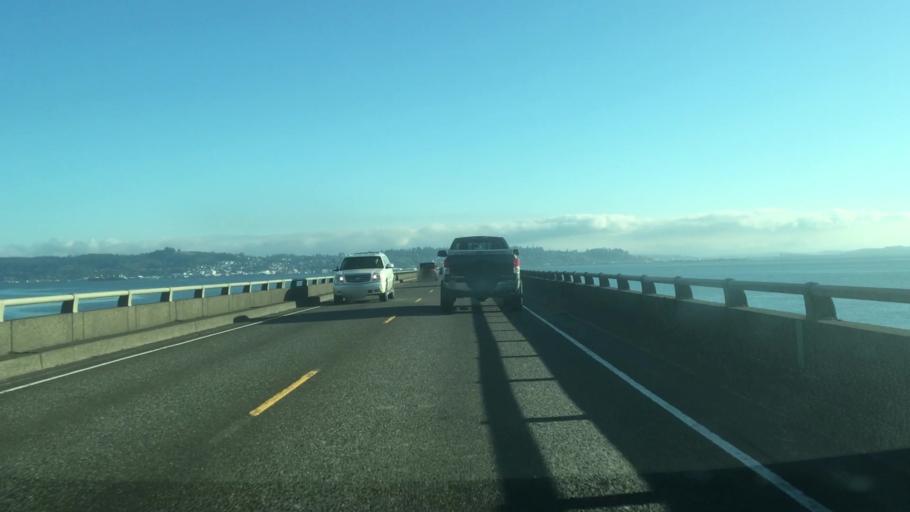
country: US
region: Oregon
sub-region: Clatsop County
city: Astoria
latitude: 46.2287
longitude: -123.8687
